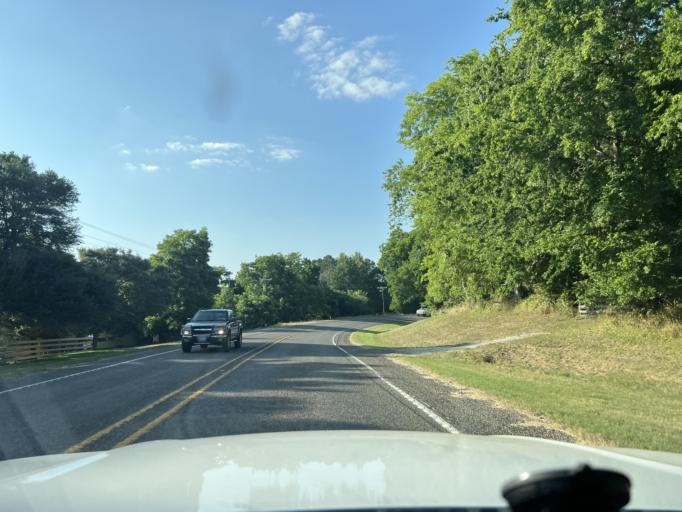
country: US
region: Texas
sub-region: Washington County
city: Brenham
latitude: 30.1494
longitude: -96.2574
